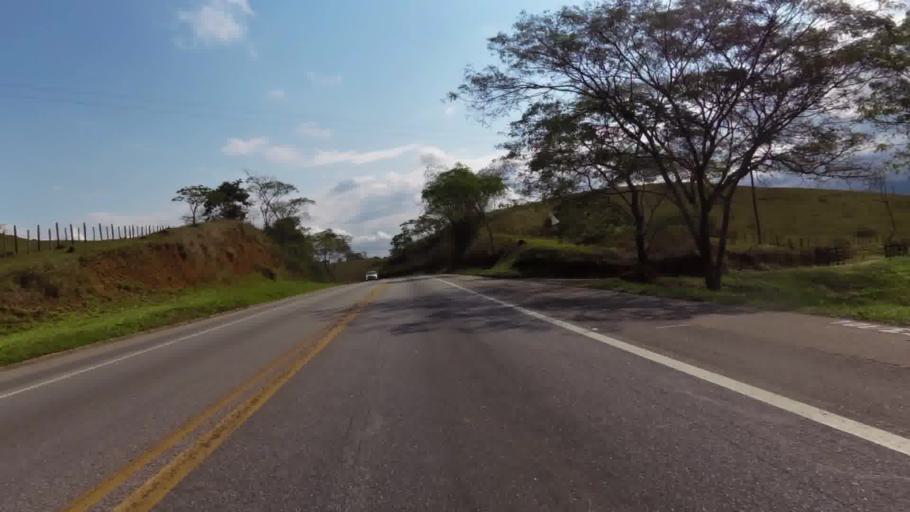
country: BR
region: Rio de Janeiro
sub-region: Macae
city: Macae
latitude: -22.2531
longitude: -41.8272
